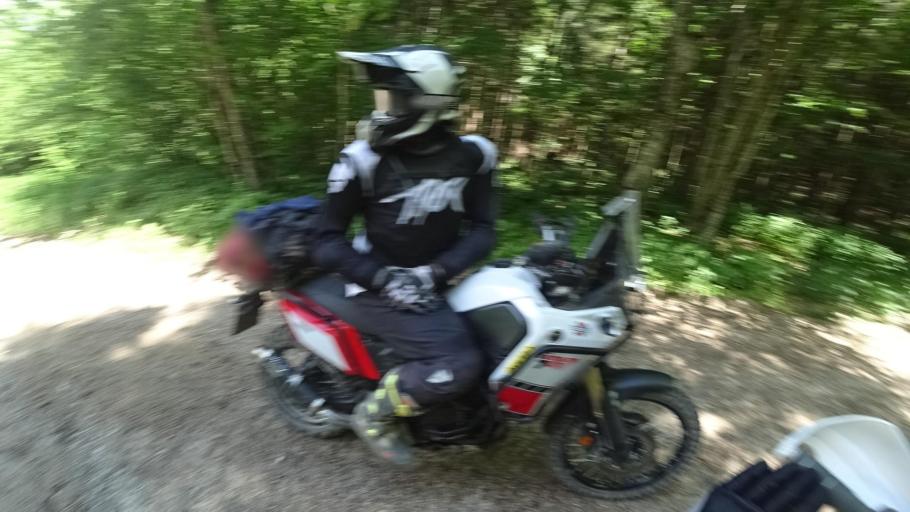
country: BA
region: Federation of Bosnia and Herzegovina
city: Ostrozac
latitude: 44.8267
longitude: 16.0062
